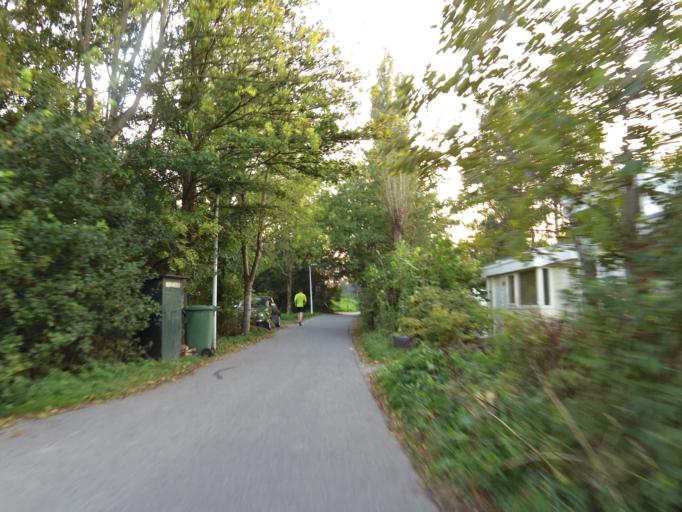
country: NL
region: South Holland
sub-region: Gemeente Leiden
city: Leiden
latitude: 52.1478
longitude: 4.5085
